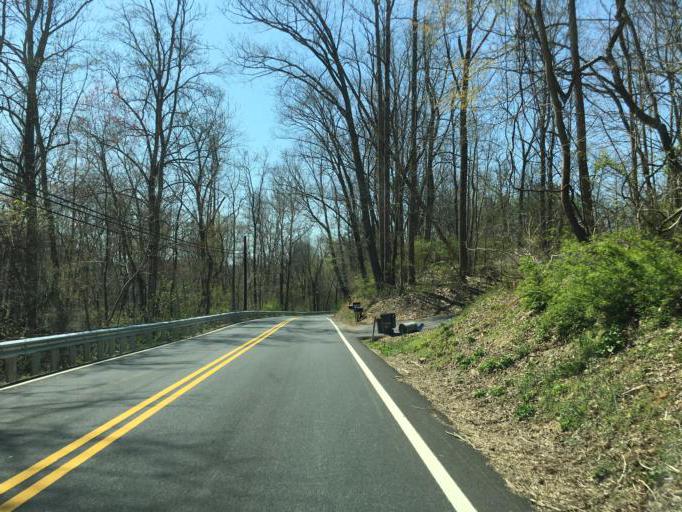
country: US
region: Maryland
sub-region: Frederick County
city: Myersville
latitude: 39.5360
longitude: -77.5320
